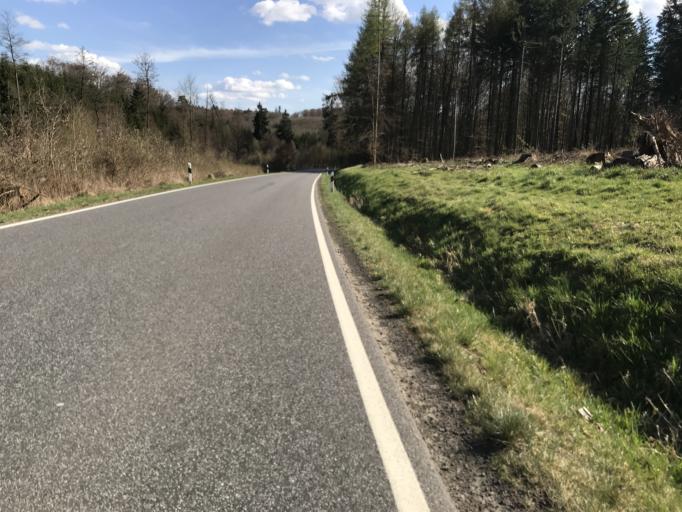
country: DE
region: Hesse
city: Beuern
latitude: 50.6475
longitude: 8.8321
